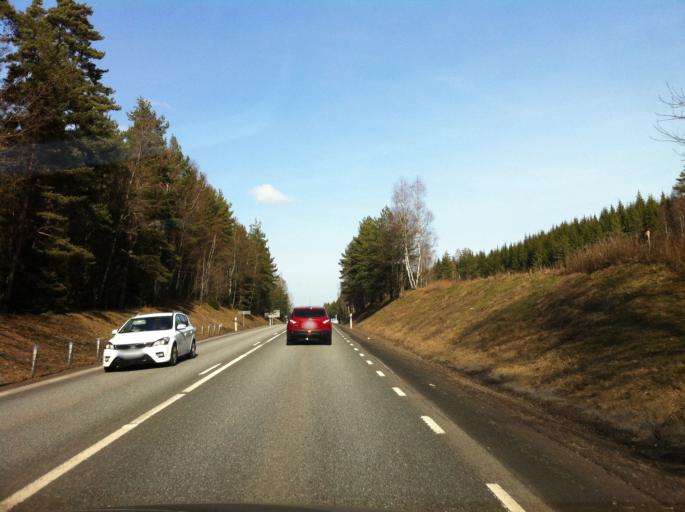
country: SE
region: Joenkoeping
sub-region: Mullsjo Kommun
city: Mullsjoe
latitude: 57.9728
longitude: 13.8333
